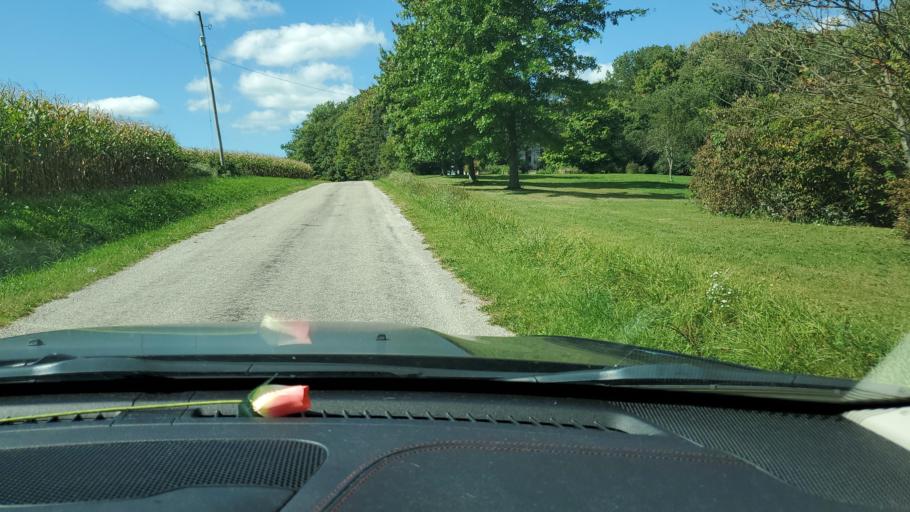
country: US
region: Ohio
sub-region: Ashtabula County
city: Andover
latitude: 41.4676
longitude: -80.5782
